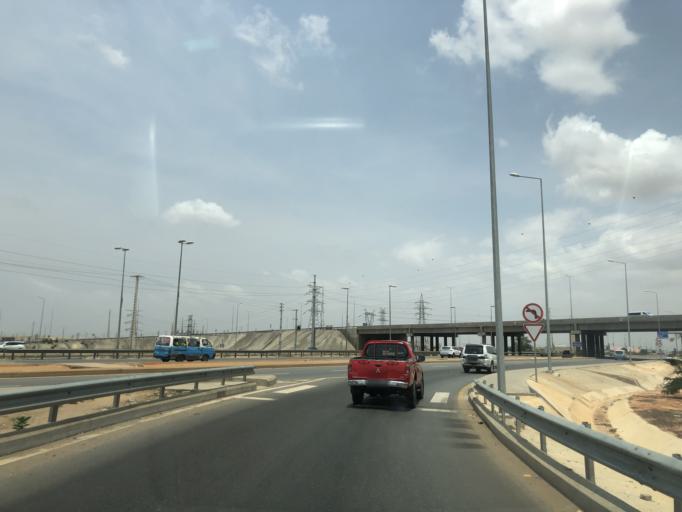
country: AO
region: Luanda
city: Luanda
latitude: -8.9739
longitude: 13.2525
